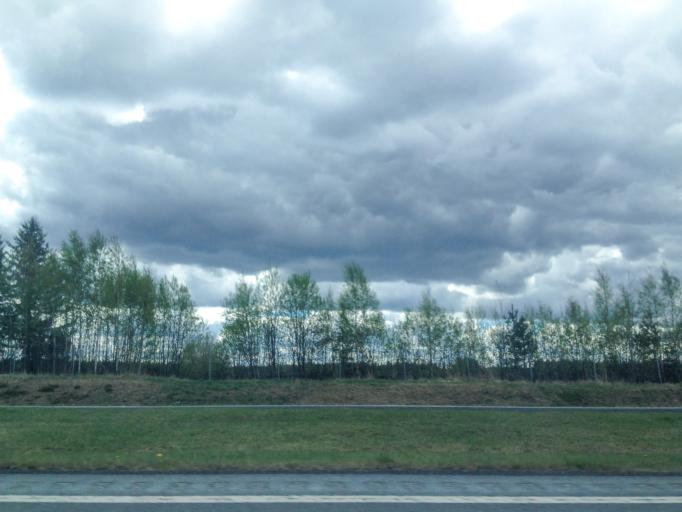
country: FI
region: Pirkanmaa
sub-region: Etelae-Pirkanmaa
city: Valkeakoski
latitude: 61.1521
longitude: 23.9871
